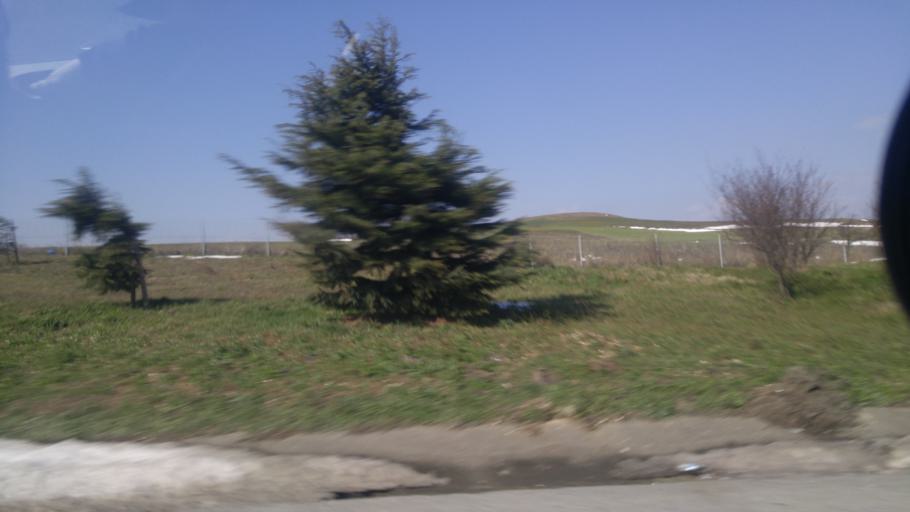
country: TR
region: Istanbul
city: Celaliye
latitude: 41.0550
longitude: 28.4564
